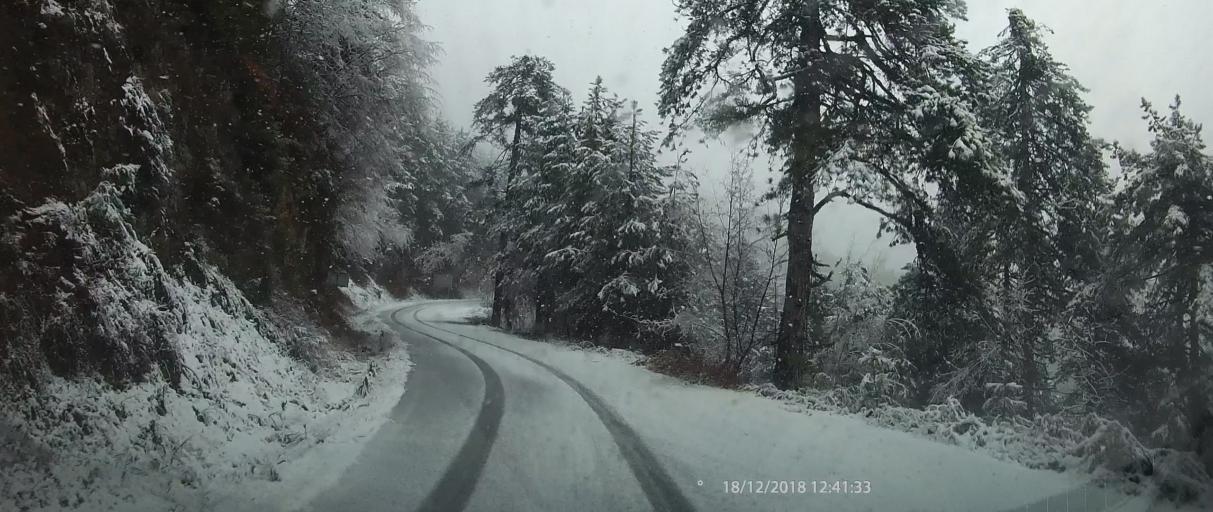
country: GR
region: Central Macedonia
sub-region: Nomos Pierias
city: Litochoro
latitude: 40.0934
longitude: 22.4198
